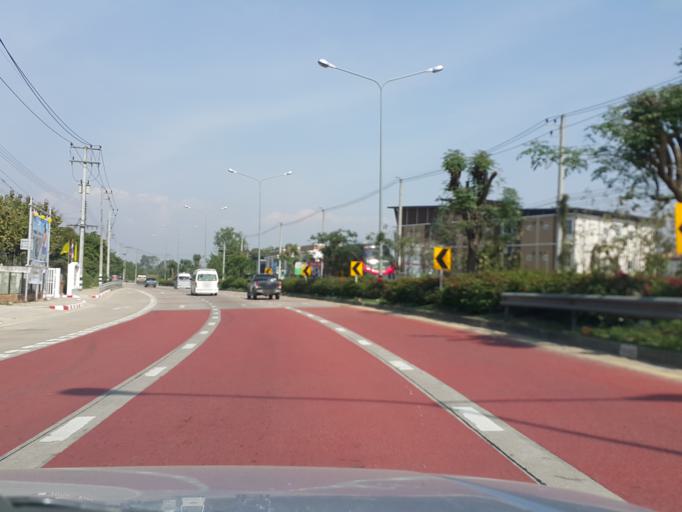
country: TH
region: Chiang Mai
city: Saraphi
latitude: 18.7448
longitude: 99.0157
